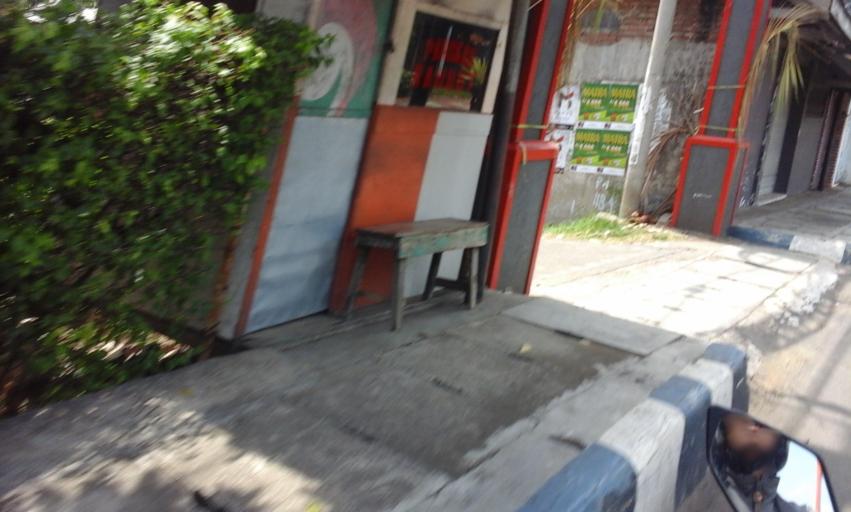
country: ID
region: East Java
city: Klatakan
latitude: -8.1824
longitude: 114.3818
